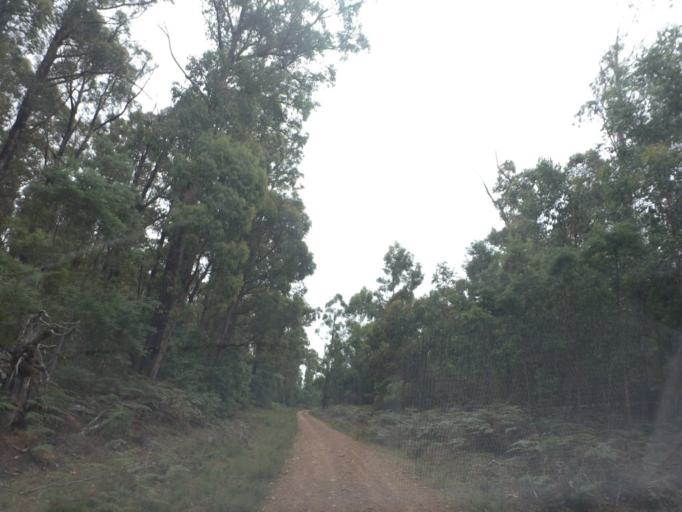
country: AU
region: Victoria
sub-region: Murrindindi
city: Alexandra
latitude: -37.3907
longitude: 145.5769
